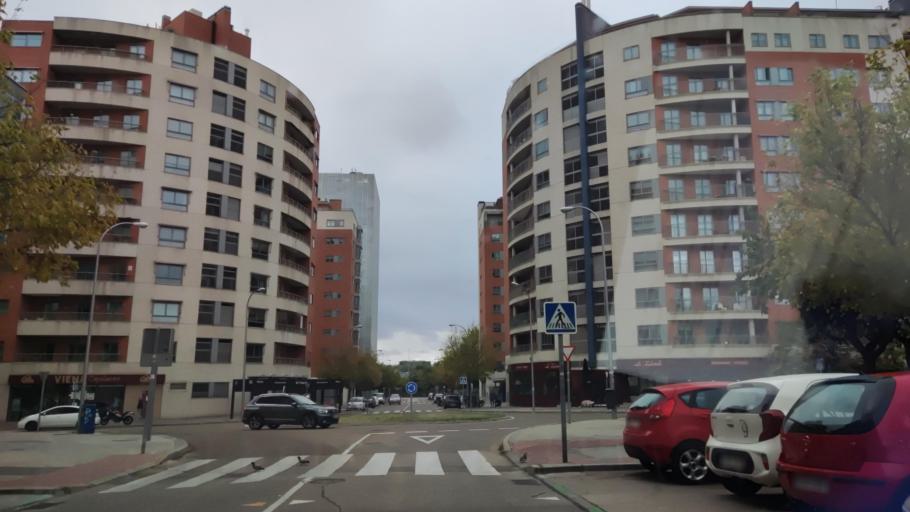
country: ES
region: Madrid
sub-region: Provincia de Madrid
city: Arganzuela
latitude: 40.3934
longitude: -3.6798
